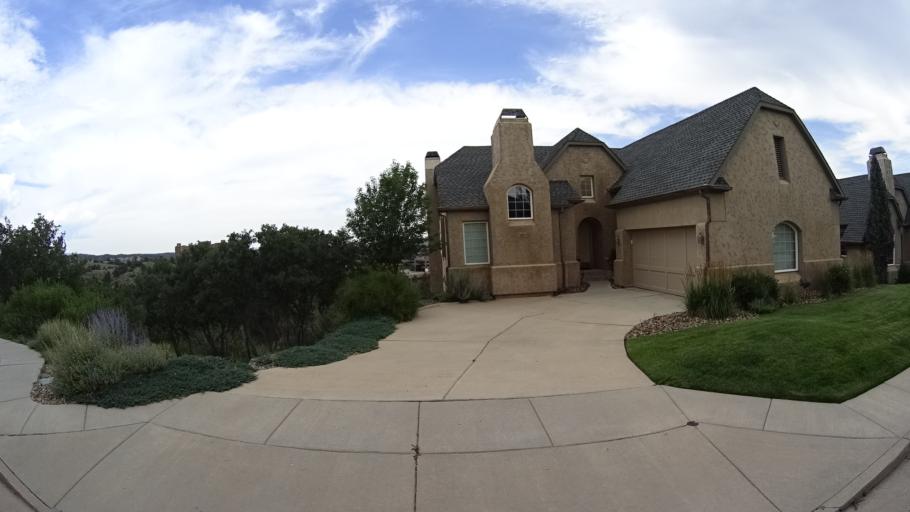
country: US
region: Colorado
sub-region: El Paso County
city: Colorado Springs
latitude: 38.9080
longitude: -104.8299
